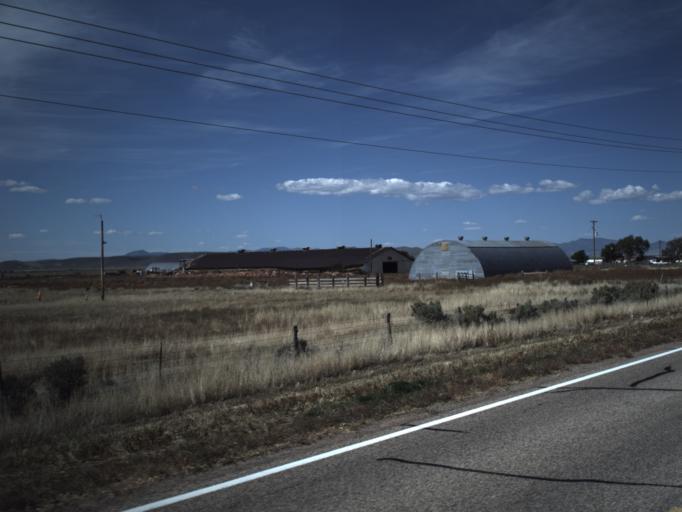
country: US
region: Utah
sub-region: Washington County
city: Enterprise
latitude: 37.6152
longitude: -113.6612
